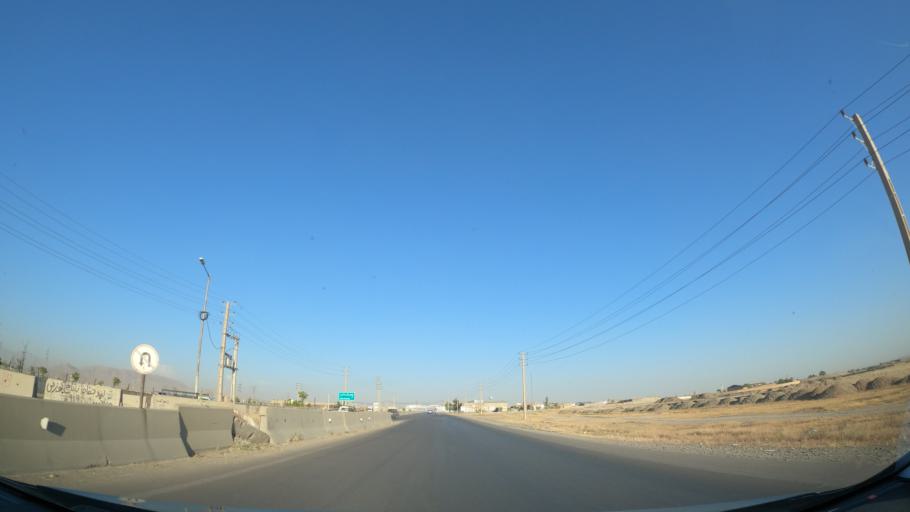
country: IR
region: Alborz
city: Hashtgerd
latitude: 35.9201
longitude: 50.7485
